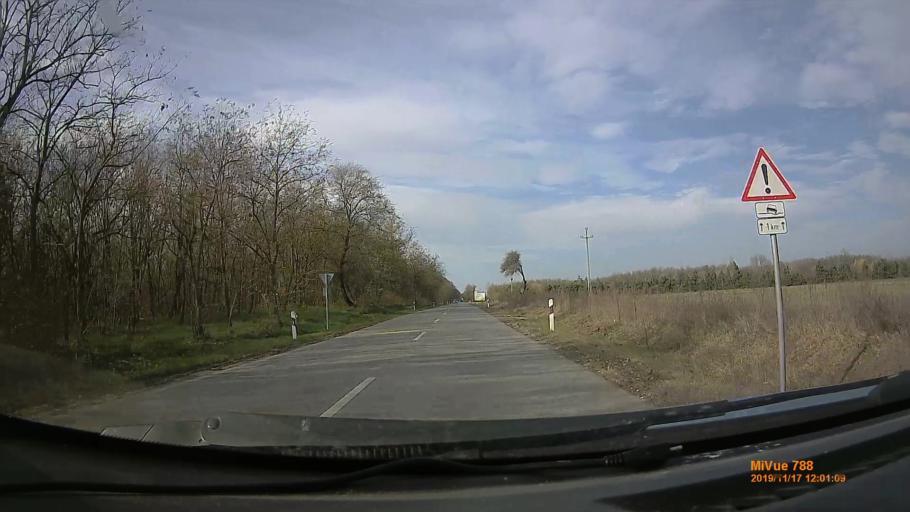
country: HU
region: Bacs-Kiskun
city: Lakitelek
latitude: 46.8816
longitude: 19.9892
